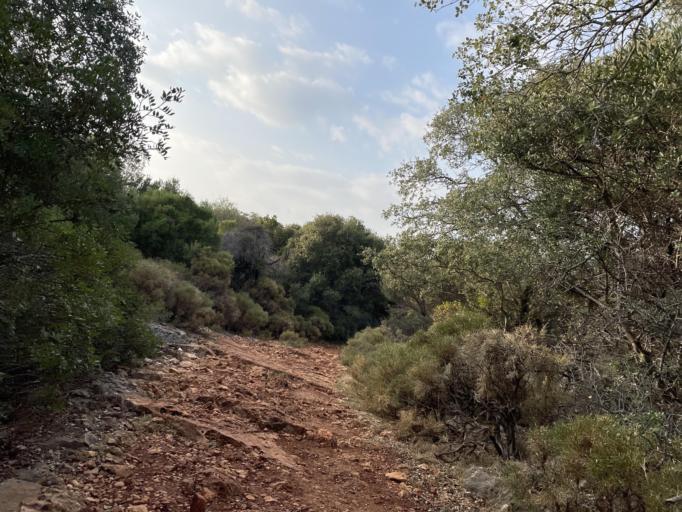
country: TR
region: Antalya
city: Kas
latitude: 36.1632
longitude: 29.6545
